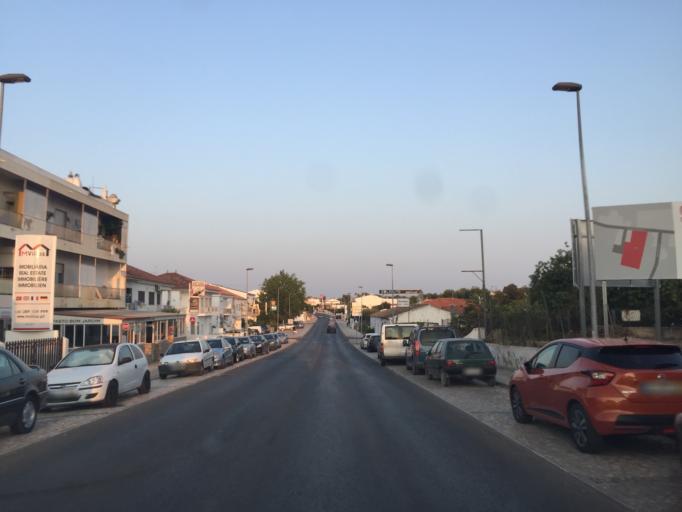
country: PT
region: Faro
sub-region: Loule
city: Almancil
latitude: 37.0850
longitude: -8.0260
